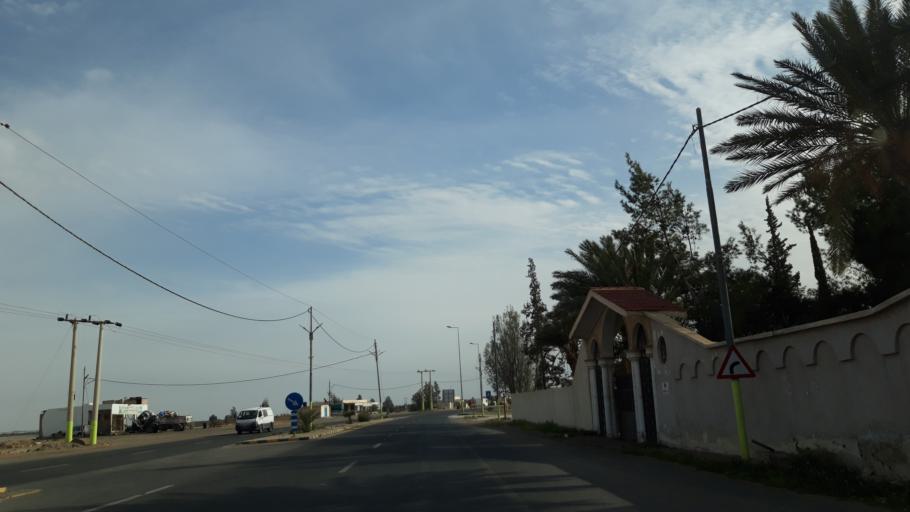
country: JO
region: Amman
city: Al Azraq ash Shamali
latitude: 31.8759
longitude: 36.8256
